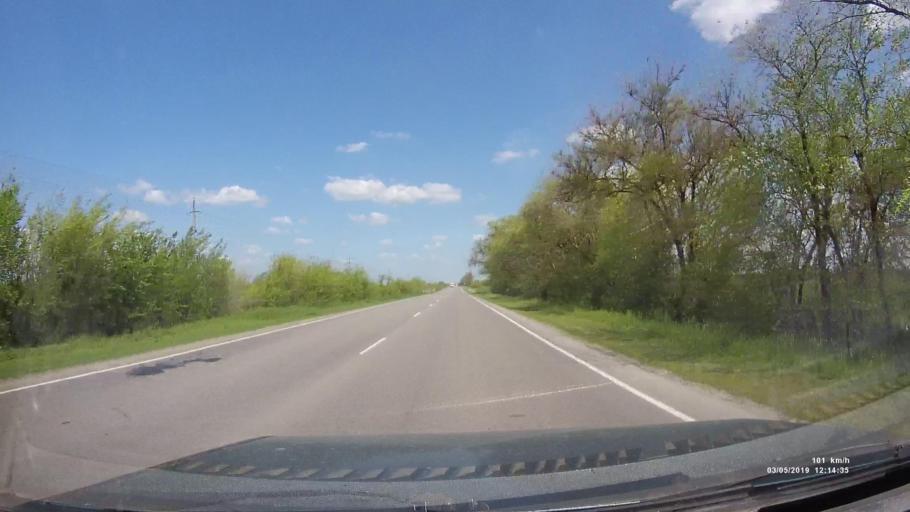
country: RU
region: Rostov
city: Melikhovskaya
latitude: 47.3462
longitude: 40.5650
